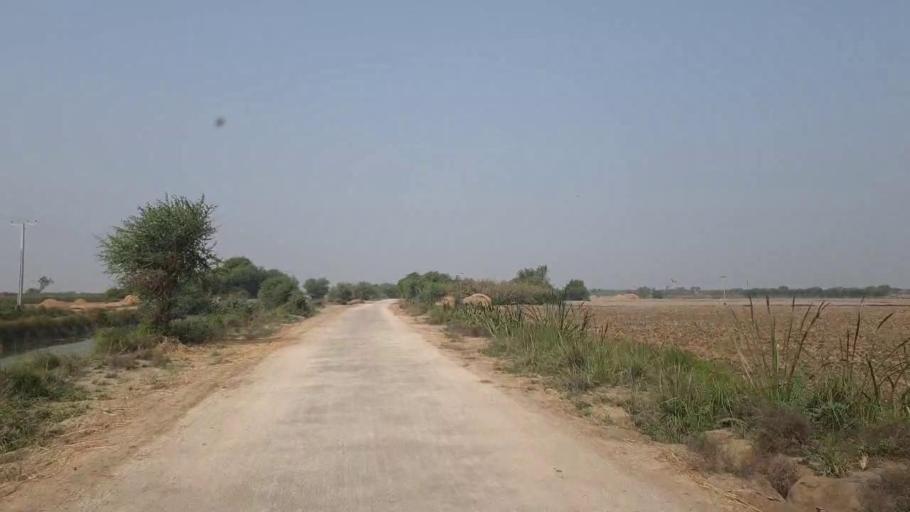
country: PK
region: Sindh
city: Kario
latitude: 24.9144
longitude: 68.6026
